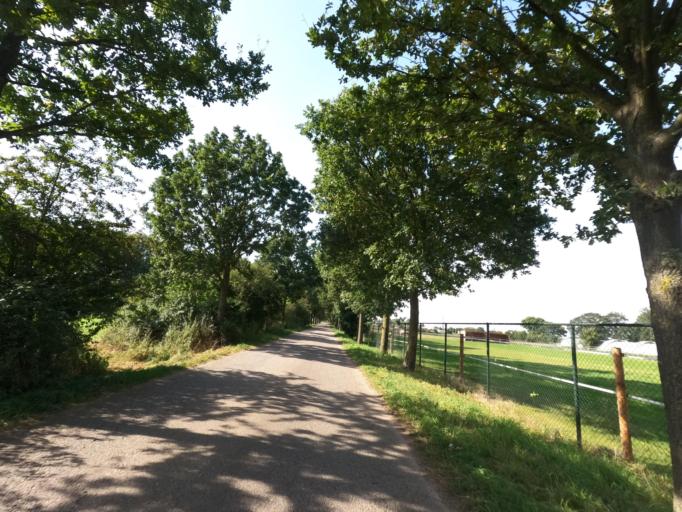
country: DE
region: North Rhine-Westphalia
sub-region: Regierungsbezirk Koln
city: Linnich
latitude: 50.9760
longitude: 6.2896
